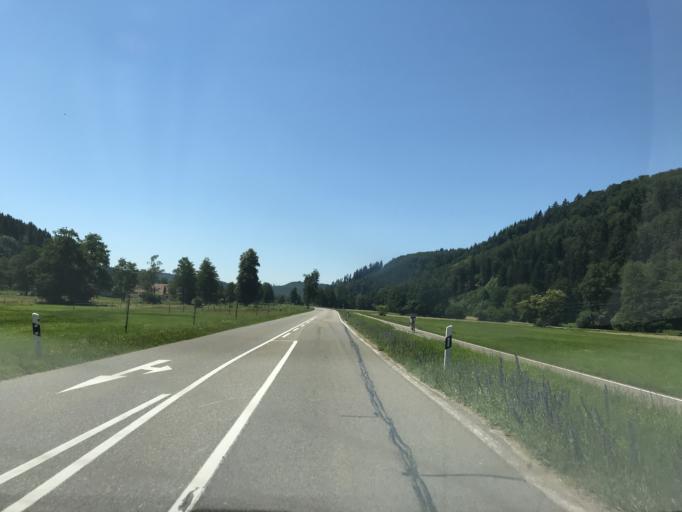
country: DE
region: Baden-Wuerttemberg
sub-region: Freiburg Region
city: Schopfheim
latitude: 47.6720
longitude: 7.8033
